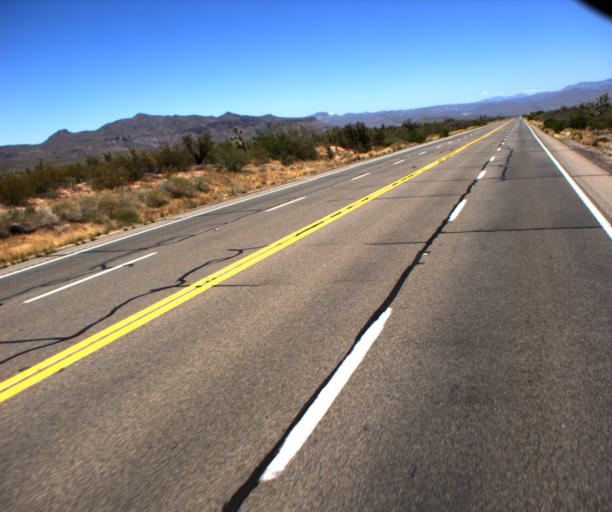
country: US
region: Arizona
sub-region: Yavapai County
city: Congress
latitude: 34.2807
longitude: -113.1025
